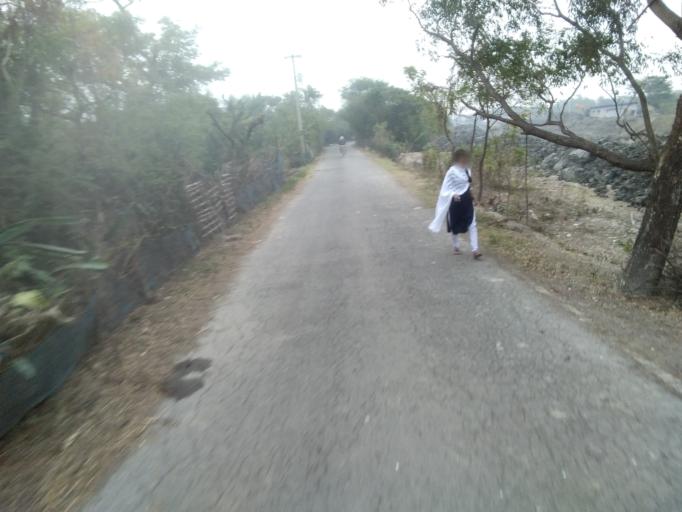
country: BD
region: Khulna
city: Satkhira
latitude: 22.5749
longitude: 89.0756
